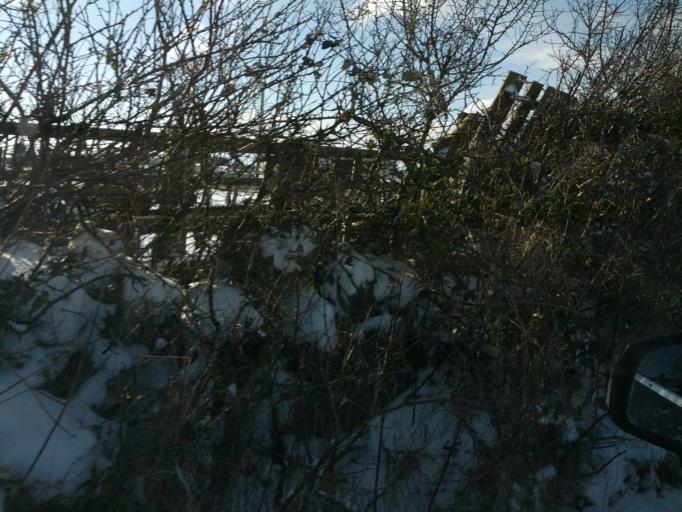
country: IE
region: Connaught
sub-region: County Galway
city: Athenry
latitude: 53.2016
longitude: -8.8087
